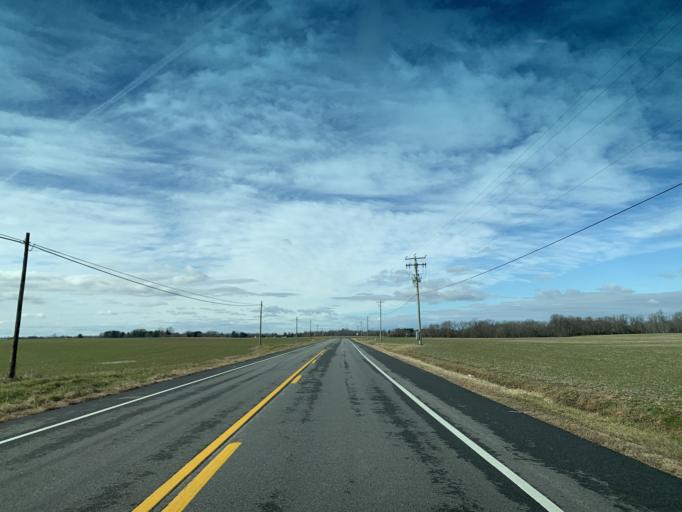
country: US
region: Maryland
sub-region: Queen Anne's County
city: Kingstown
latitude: 39.3235
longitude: -76.0246
